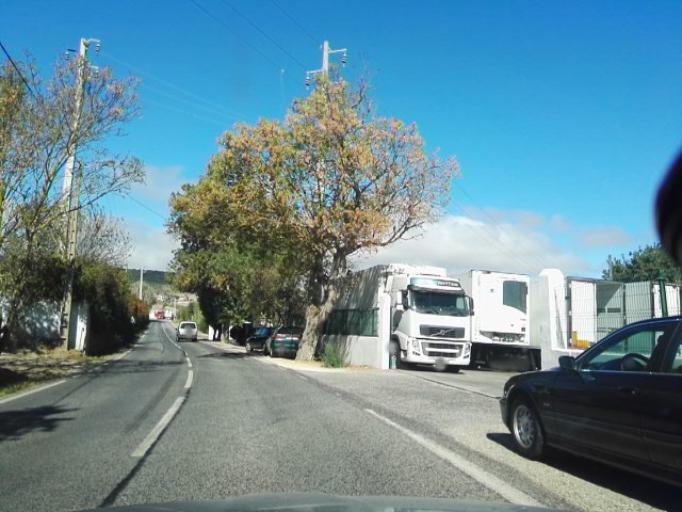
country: PT
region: Lisbon
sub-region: Arruda Dos Vinhos
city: Arruda dos Vinhos
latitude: 38.9779
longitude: -9.0693
